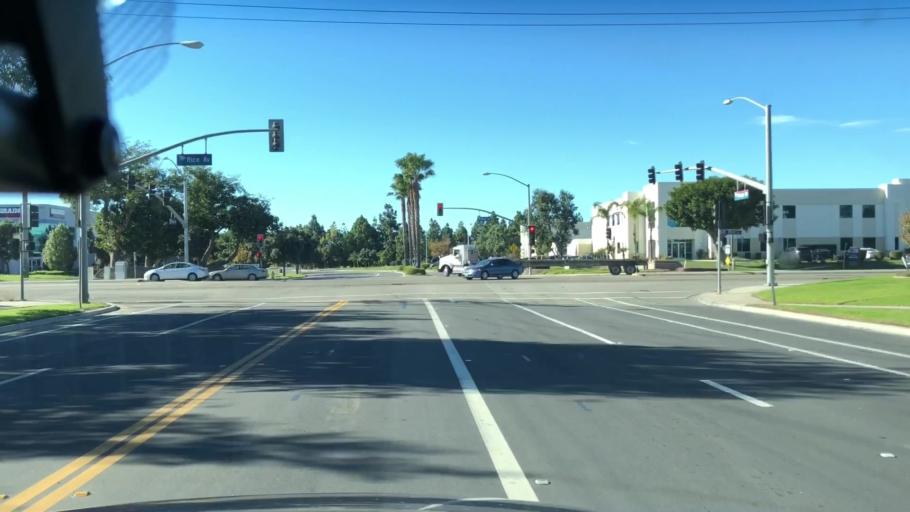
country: US
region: California
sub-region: Ventura County
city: Oxnard
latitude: 34.2019
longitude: -119.1416
